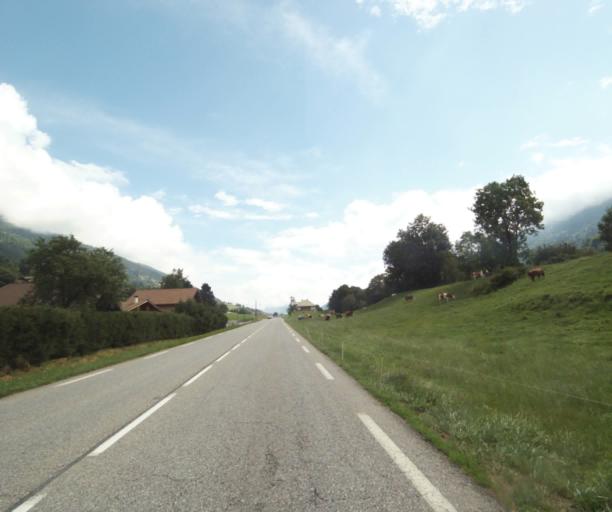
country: FR
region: Rhone-Alpes
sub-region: Departement de la Haute-Savoie
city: Thones
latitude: 45.9008
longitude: 6.3521
